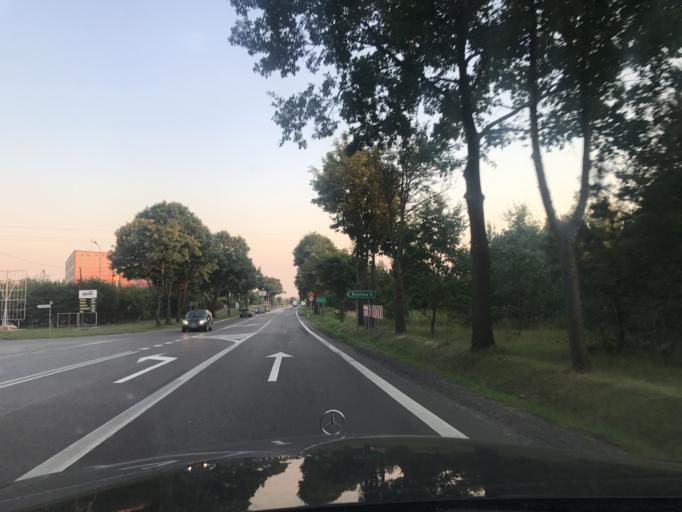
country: PL
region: Lublin Voivodeship
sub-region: Powiat lubelski
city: Niemce
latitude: 51.3755
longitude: 22.6342
